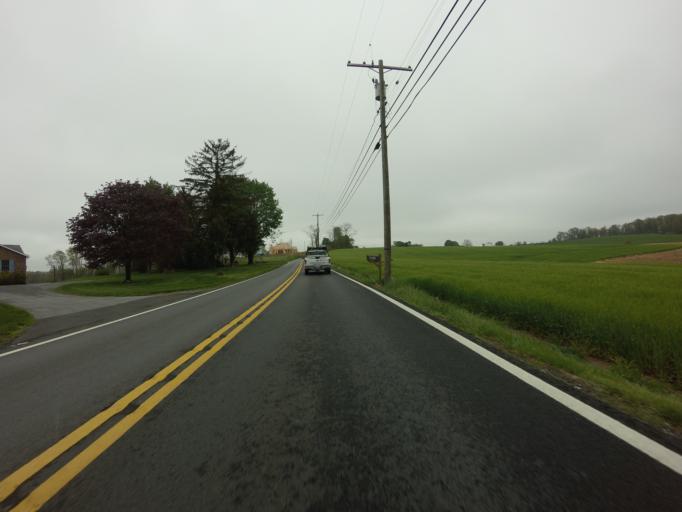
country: US
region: Maryland
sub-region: Carroll County
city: Hampstead
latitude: 39.6045
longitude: -76.8413
